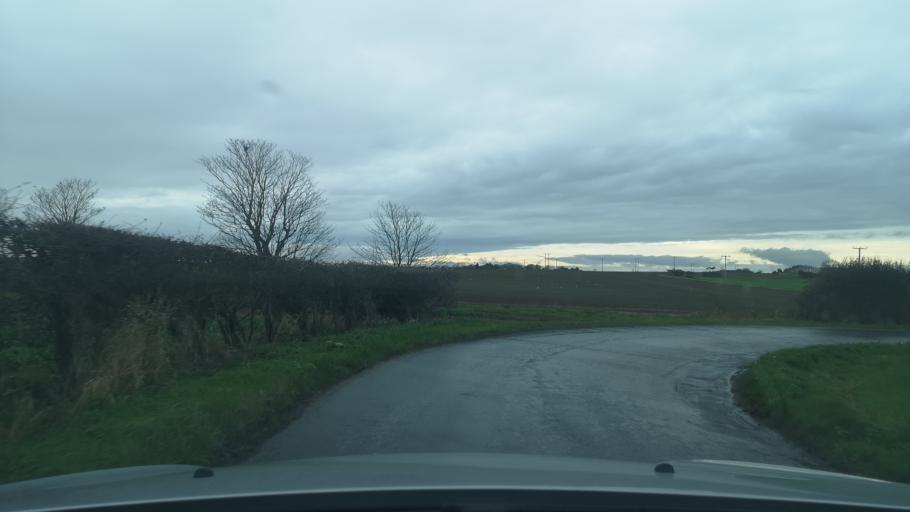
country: GB
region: England
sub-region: East Riding of Yorkshire
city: Holmpton
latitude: 53.6776
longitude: 0.0790
